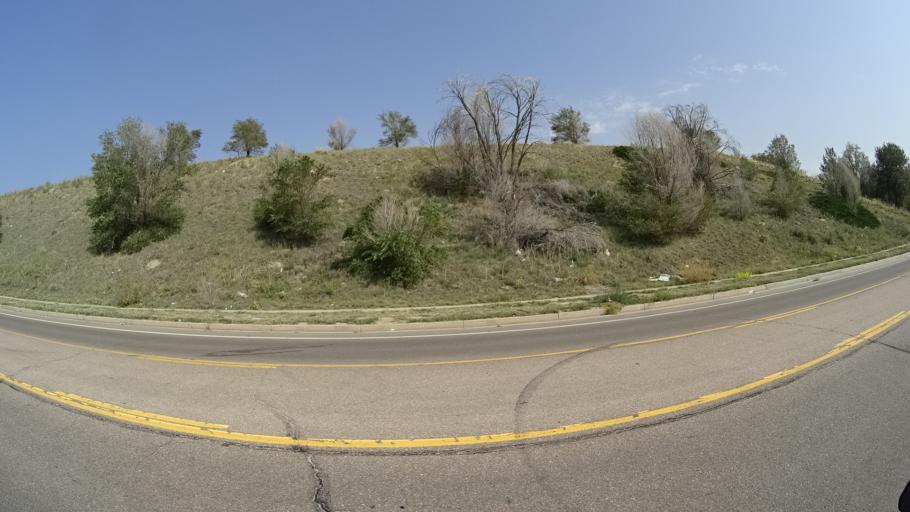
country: US
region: Colorado
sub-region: El Paso County
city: Cimarron Hills
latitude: 38.8356
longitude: -104.7551
